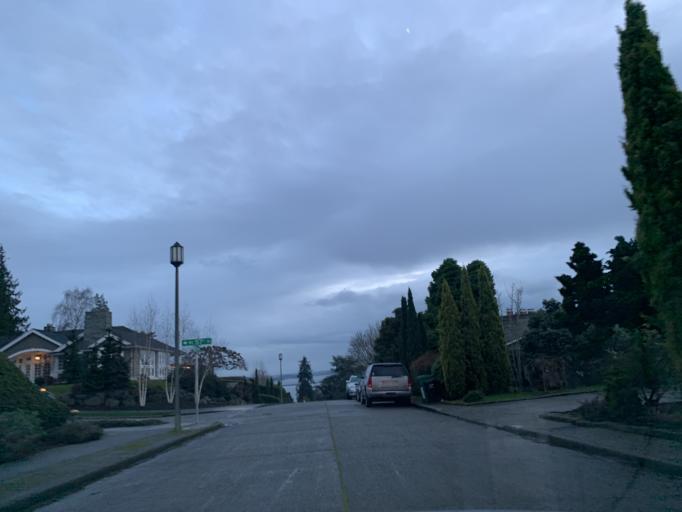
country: US
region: Washington
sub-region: King County
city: Yarrow Point
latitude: 47.6702
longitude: -122.2635
